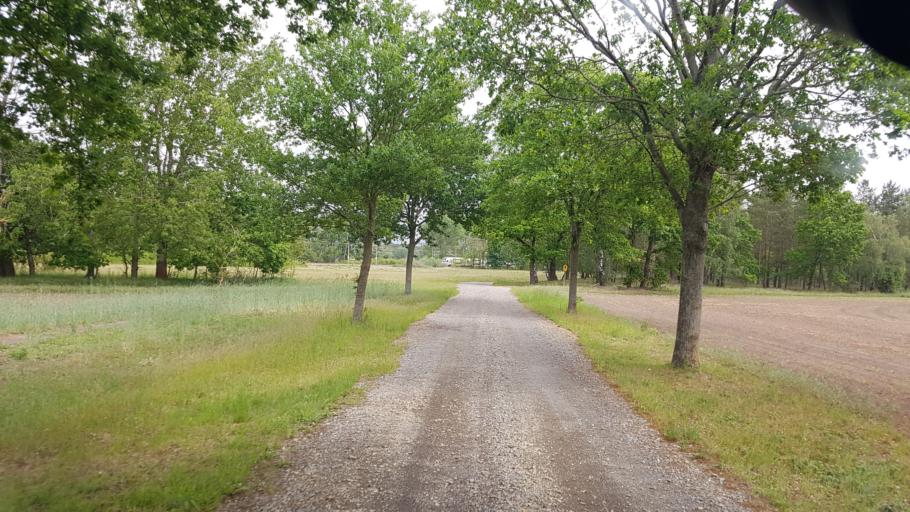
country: DE
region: Brandenburg
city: Schonewalde
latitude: 51.7114
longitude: 13.6013
